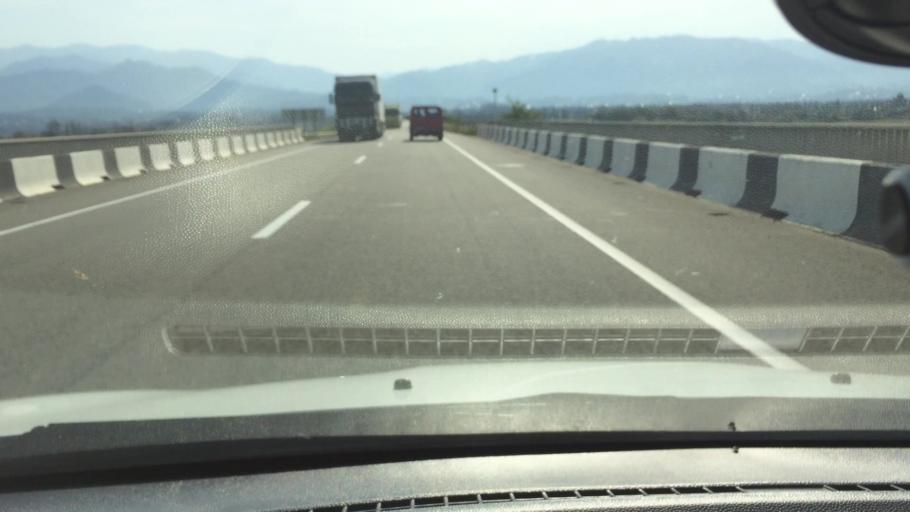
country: GE
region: Ajaria
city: Ochkhamuri
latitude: 41.8715
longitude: 41.8302
